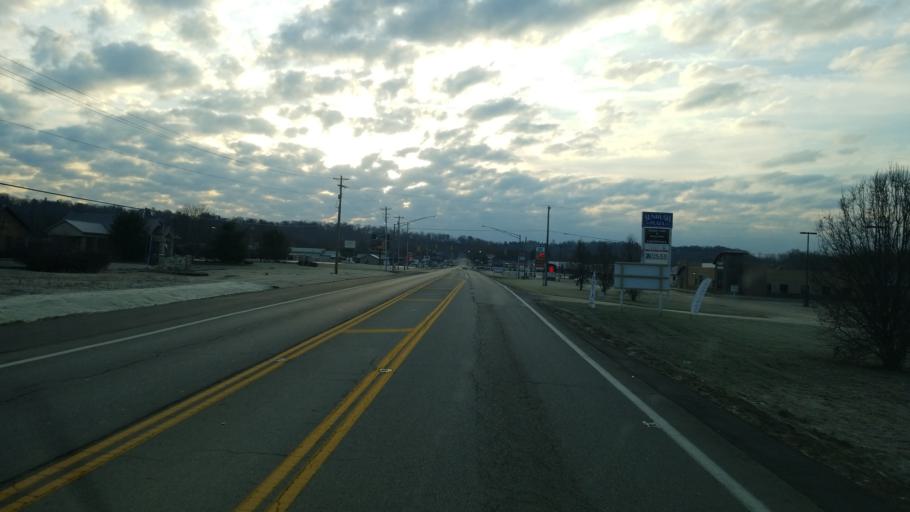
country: US
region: Ohio
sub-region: Ross County
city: North Fork Village
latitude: 39.3468
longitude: -83.0404
